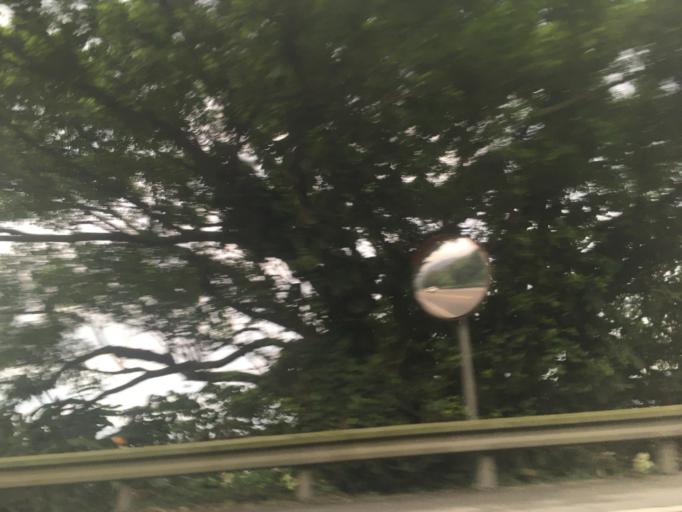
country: TW
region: Taiwan
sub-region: Keelung
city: Keelung
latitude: 24.9546
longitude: 121.9169
